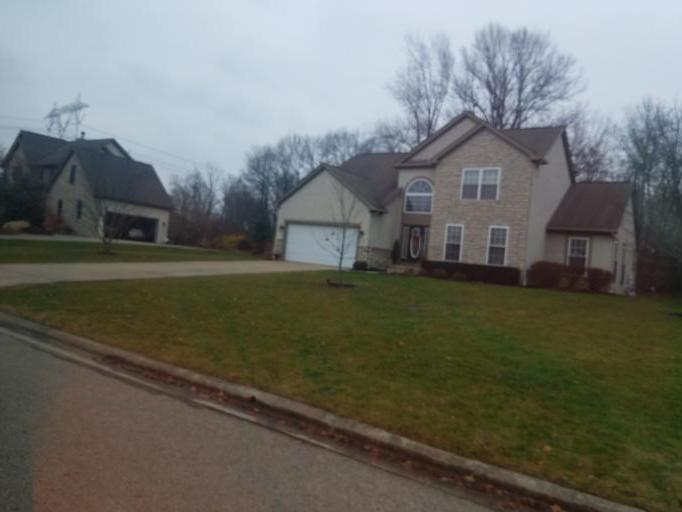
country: US
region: Ohio
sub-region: Delaware County
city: Lewis Center
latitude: 40.1808
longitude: -82.9585
